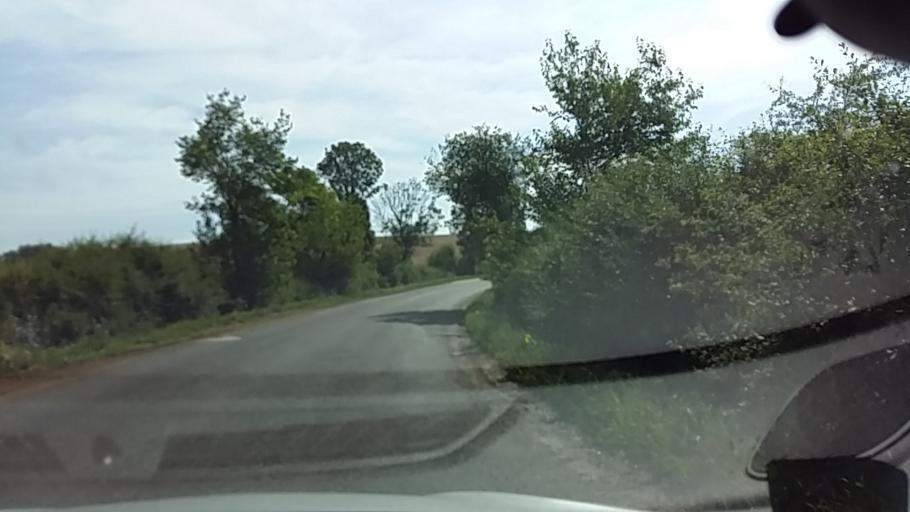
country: HU
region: Heves
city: Domoszlo
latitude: 47.7745
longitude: 20.1432
